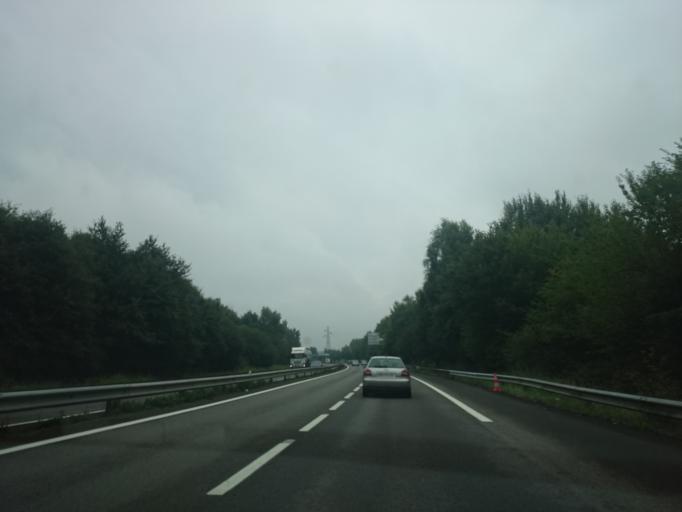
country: FR
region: Pays de la Loire
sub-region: Departement de la Loire-Atlantique
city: Orvault
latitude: 47.2806
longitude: -1.6028
